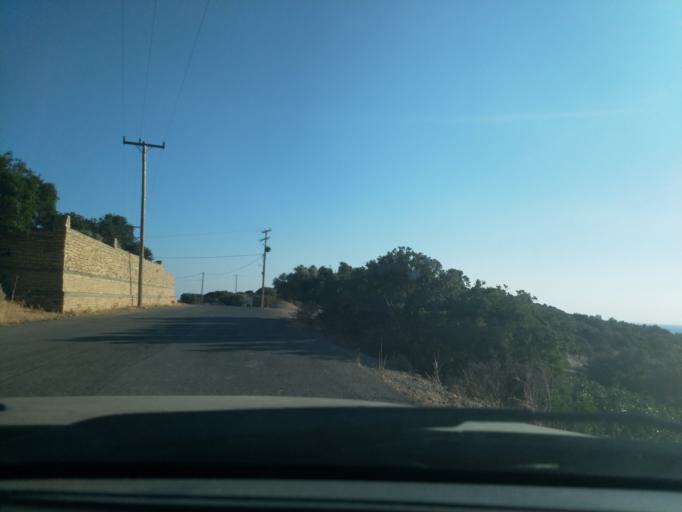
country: GR
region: Crete
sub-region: Nomos Rethymnis
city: Agia Galini
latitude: 35.1226
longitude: 24.5587
